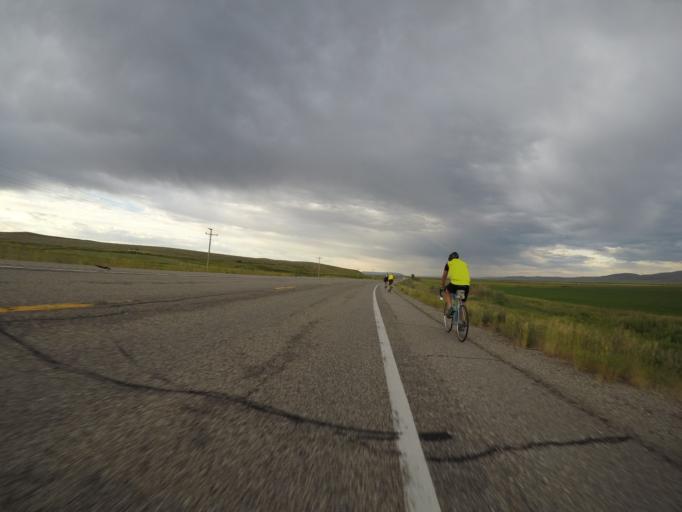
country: US
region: Utah
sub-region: Rich County
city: Randolph
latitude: 41.9755
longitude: -110.9442
